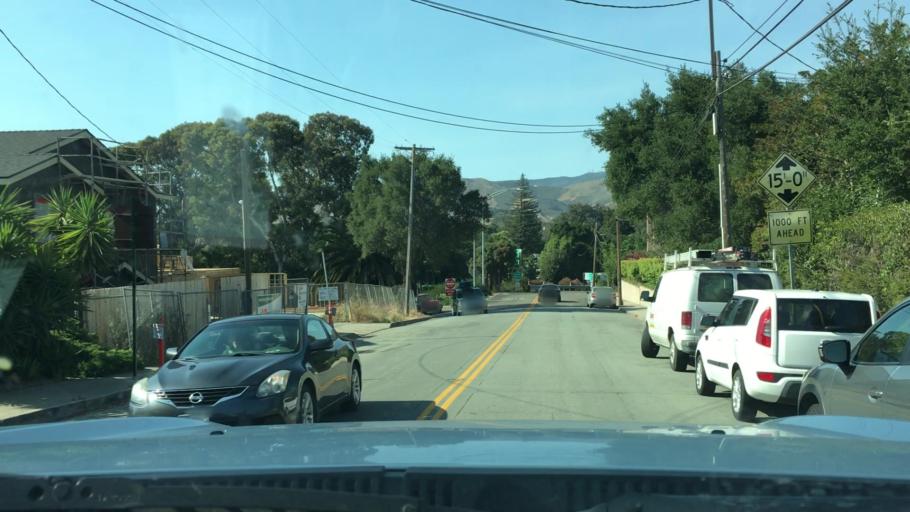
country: US
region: California
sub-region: San Luis Obispo County
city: San Luis Obispo
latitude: 35.2869
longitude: -120.6614
